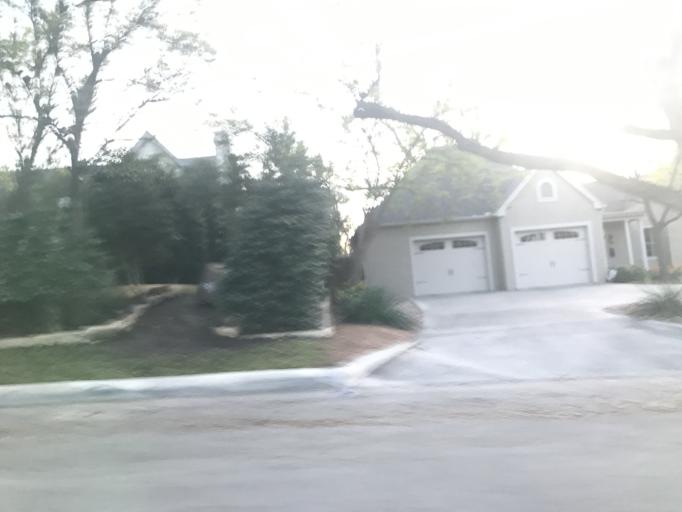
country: US
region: Texas
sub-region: Tom Green County
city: San Angelo
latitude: 31.4557
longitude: -100.4496
